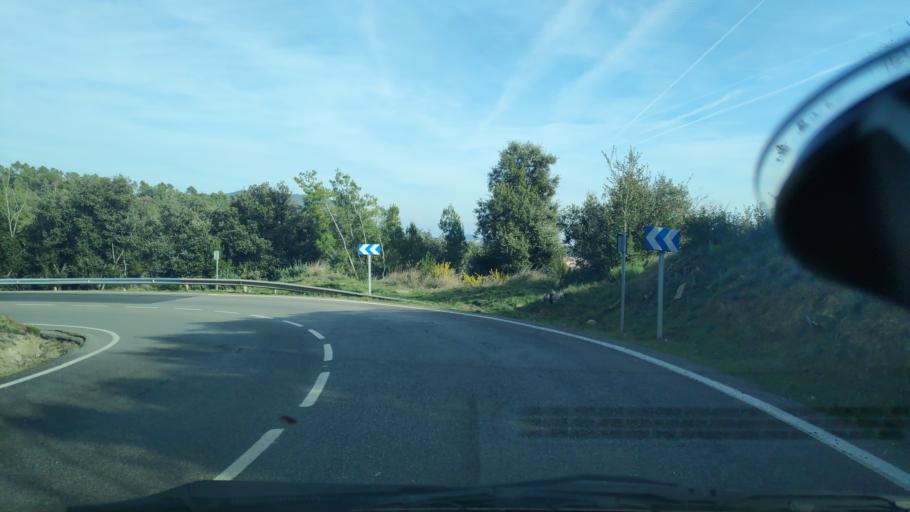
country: ES
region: Catalonia
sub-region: Provincia de Barcelona
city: Castellar del Valles
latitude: 41.6006
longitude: 2.0615
